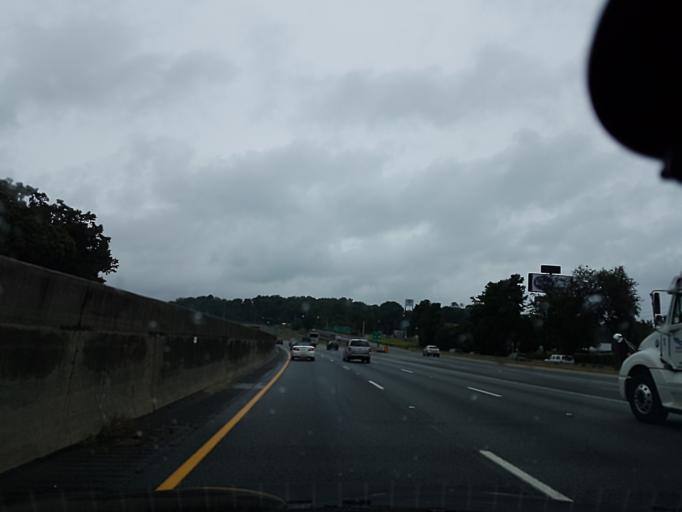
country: US
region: Georgia
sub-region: DeKalb County
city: Doraville
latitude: 33.8824
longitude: -84.2500
